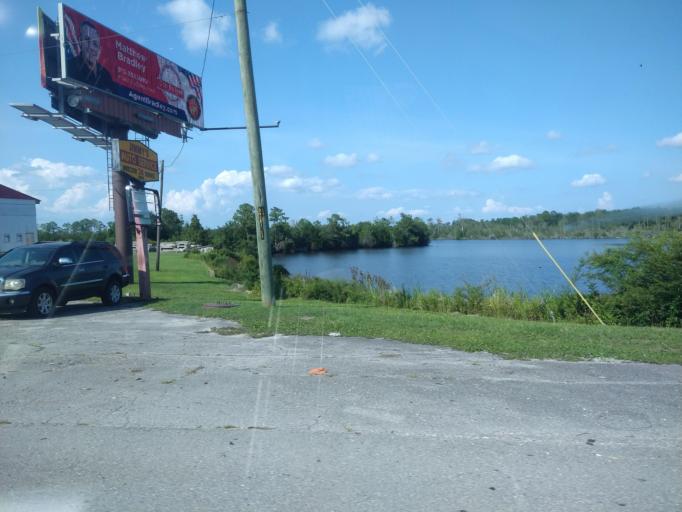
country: US
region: North Carolina
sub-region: Onslow County
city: Piney Green
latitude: 34.7352
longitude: -77.3543
